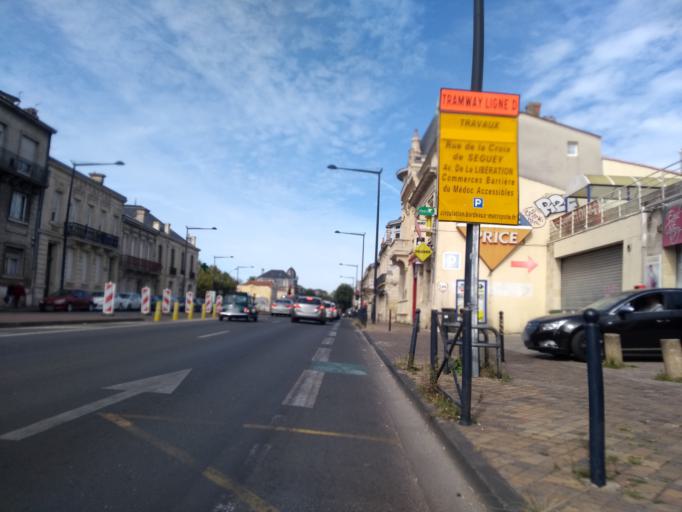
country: FR
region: Aquitaine
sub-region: Departement de la Gironde
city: Bordeaux
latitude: 44.8408
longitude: -0.5993
